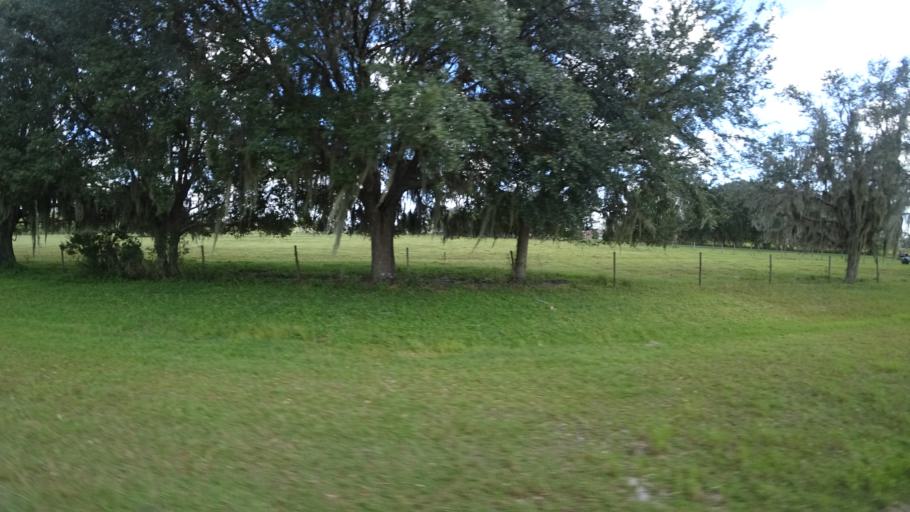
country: US
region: Florida
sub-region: Hardee County
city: Wauchula
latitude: 27.4845
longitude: -82.0794
